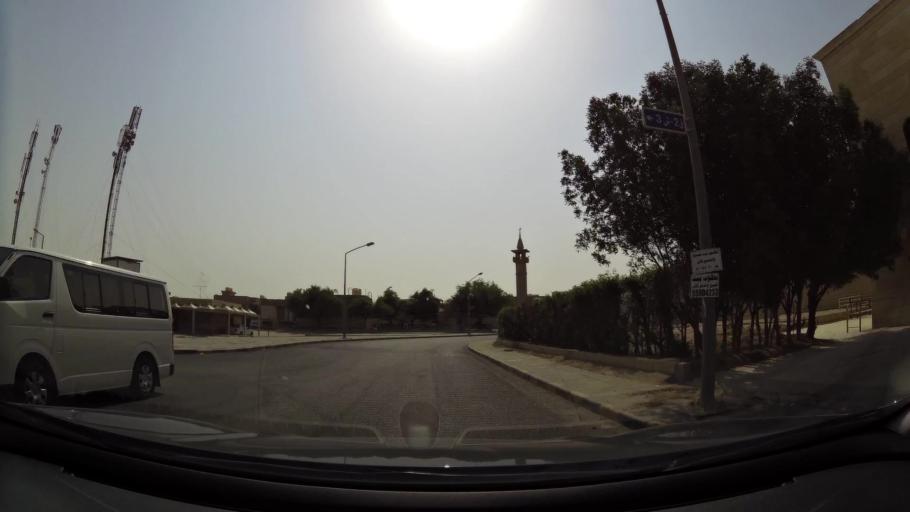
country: KW
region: Muhafazat al Jahra'
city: Al Jahra'
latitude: 29.3237
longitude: 47.6575
